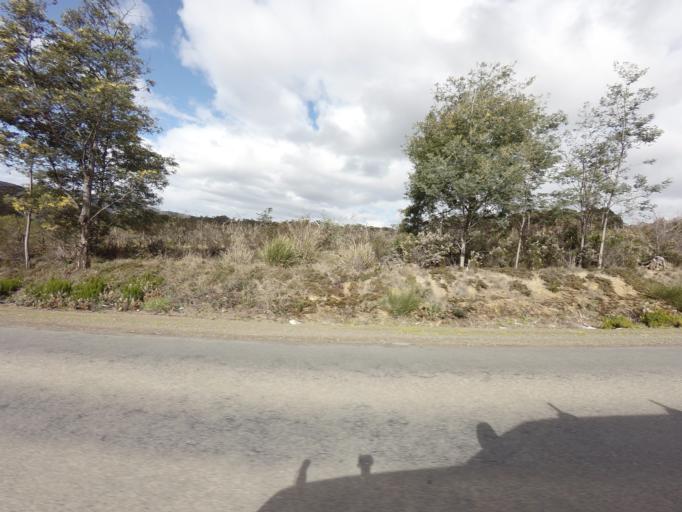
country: AU
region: Tasmania
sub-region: Huon Valley
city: Geeveston
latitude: -43.1931
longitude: 146.9581
